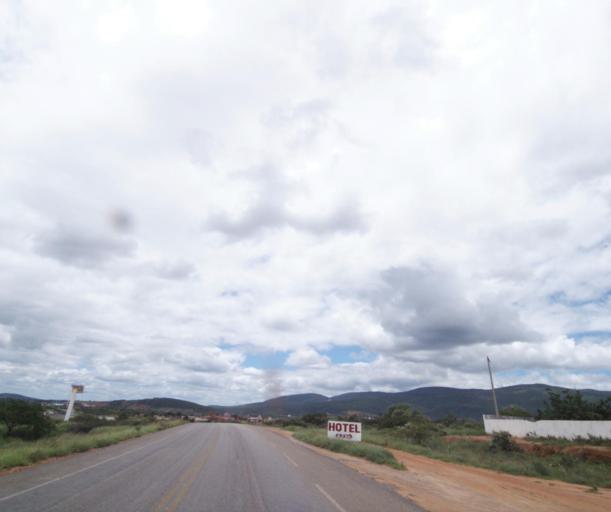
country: BR
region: Bahia
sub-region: Brumado
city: Brumado
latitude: -14.2186
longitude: -41.6643
